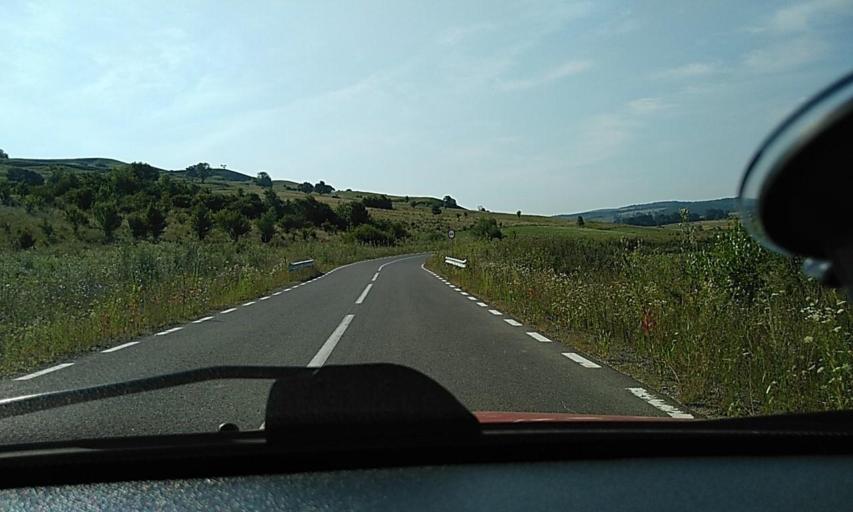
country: RO
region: Brasov
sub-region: Comuna Bunesti
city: Bunesti
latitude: 46.0811
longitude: 25.0657
